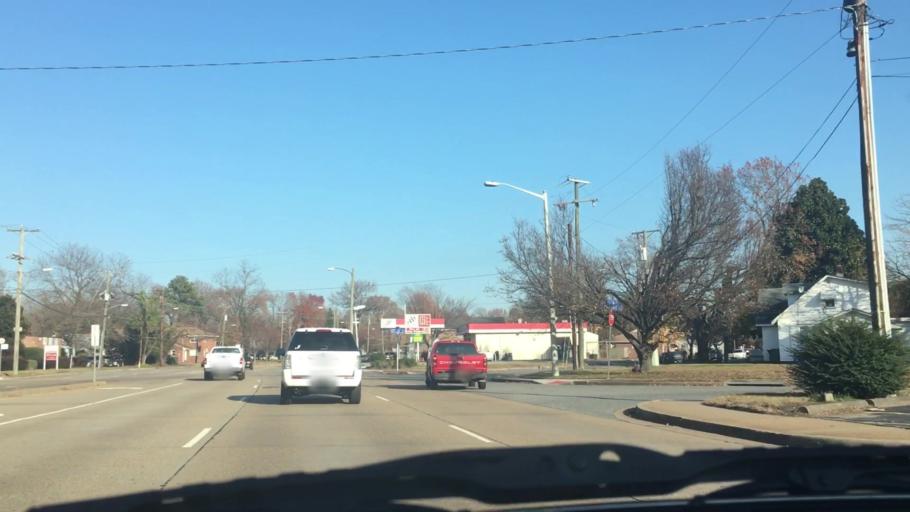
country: US
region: Virginia
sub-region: City of Norfolk
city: Norfolk
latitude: 36.9173
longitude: -76.2660
